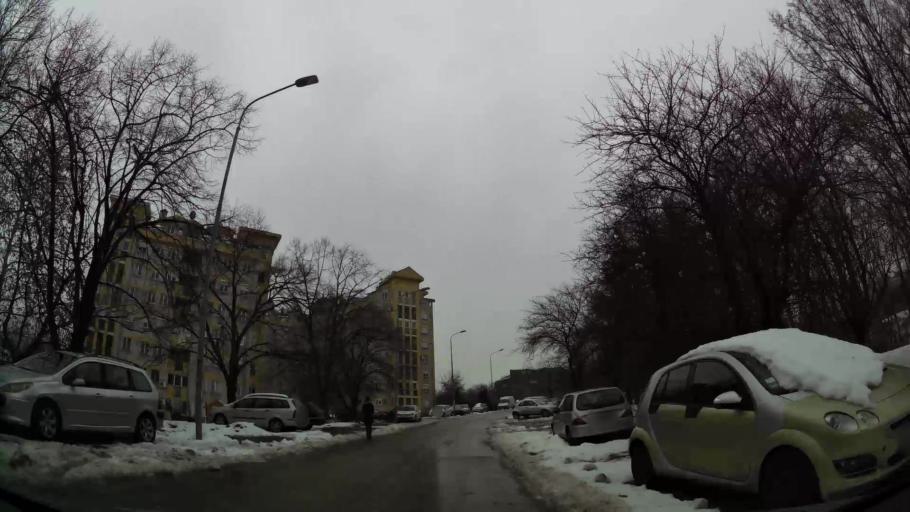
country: RS
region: Central Serbia
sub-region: Belgrade
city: Vozdovac
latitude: 44.7510
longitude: 20.4985
